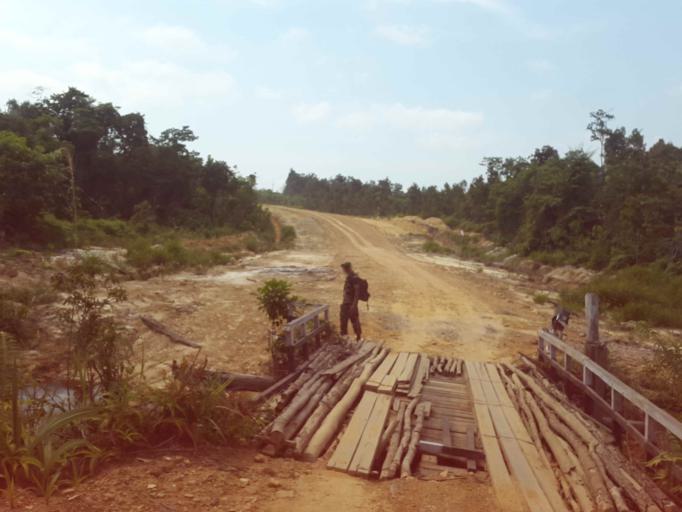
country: MY
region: Sarawak
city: Simanggang
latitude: 0.7820
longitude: 111.6756
